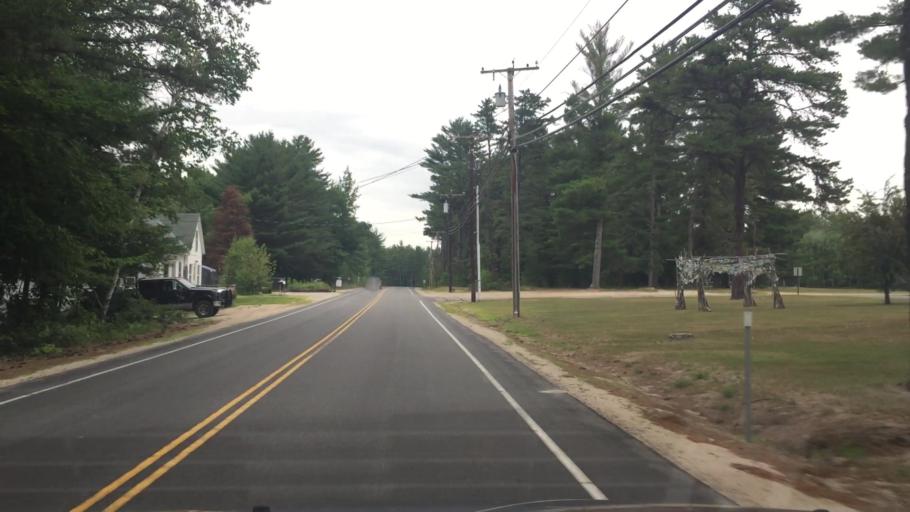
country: US
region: New Hampshire
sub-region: Carroll County
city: Tamworth
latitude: 43.8361
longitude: -71.2657
